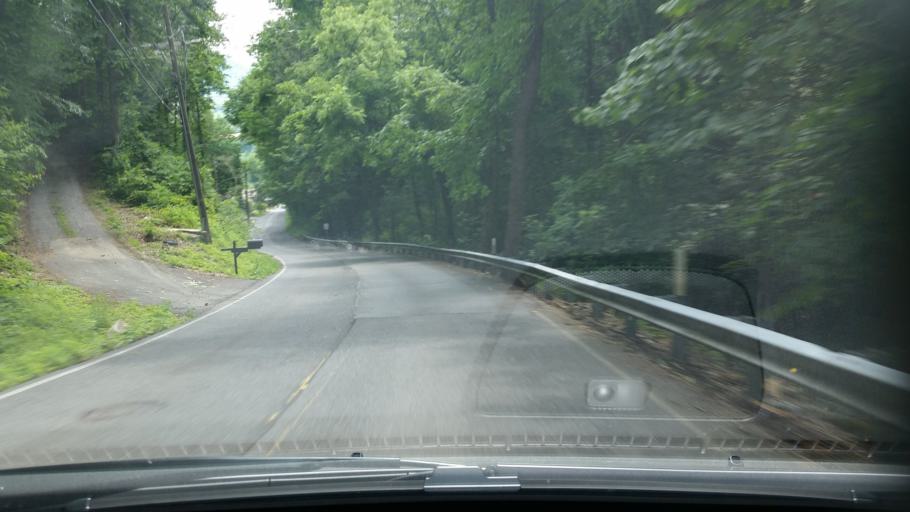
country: US
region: Tennessee
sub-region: Sevier County
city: Gatlinburg
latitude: 35.7066
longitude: -83.5323
